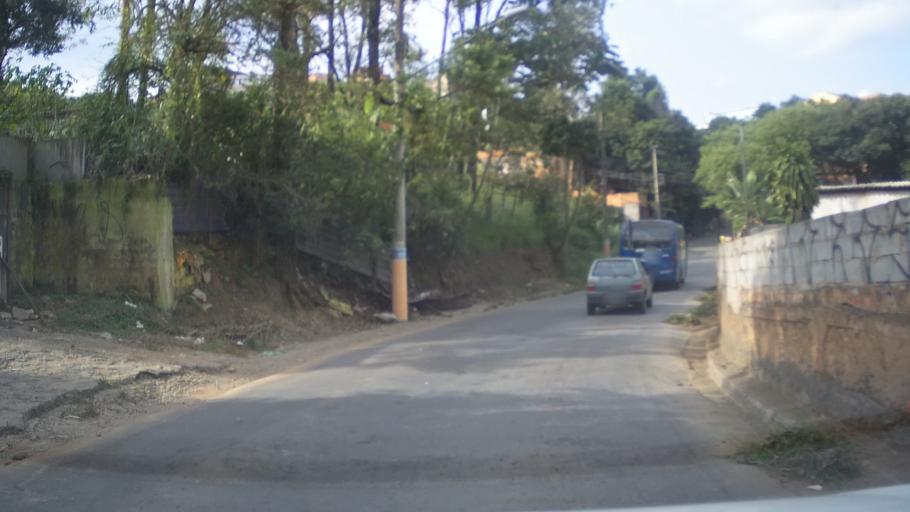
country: BR
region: Sao Paulo
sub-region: Guarulhos
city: Guarulhos
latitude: -23.4057
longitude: -46.5168
